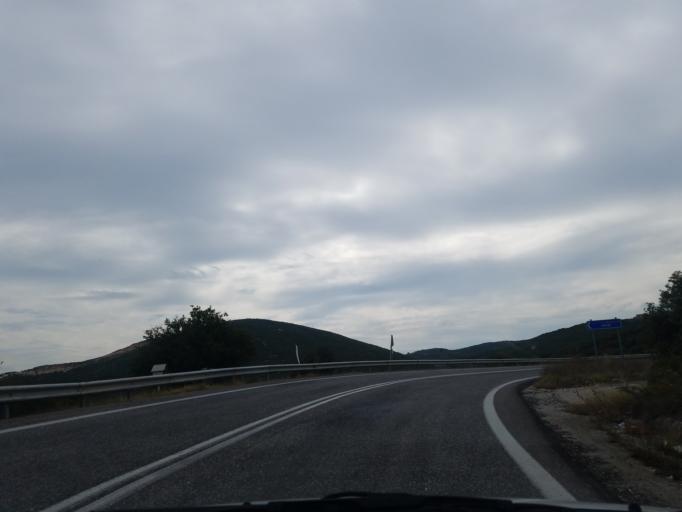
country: GR
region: Central Greece
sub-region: Nomos Fthiotidos
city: Domokos
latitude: 39.1457
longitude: 22.3138
